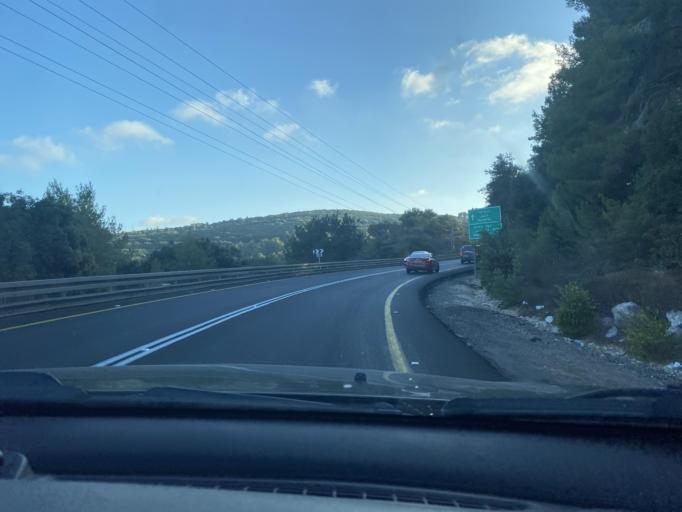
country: IL
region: Northern District
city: Kefar Weradim
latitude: 32.9928
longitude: 35.2838
